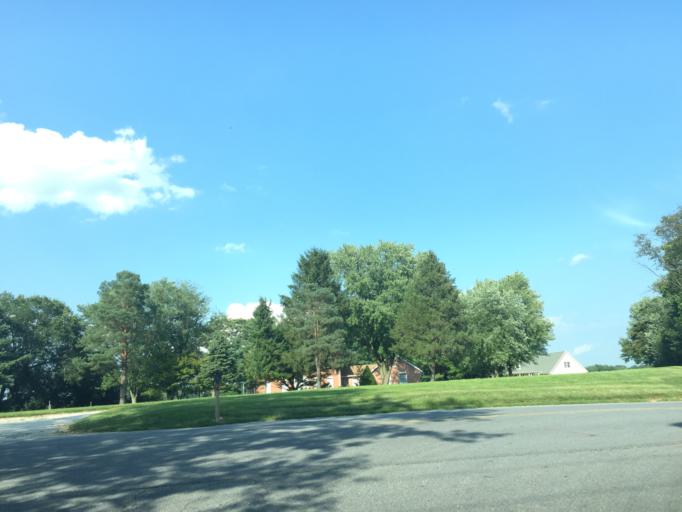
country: US
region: Maryland
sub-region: Carroll County
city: Hampstead
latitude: 39.6449
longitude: -76.8119
